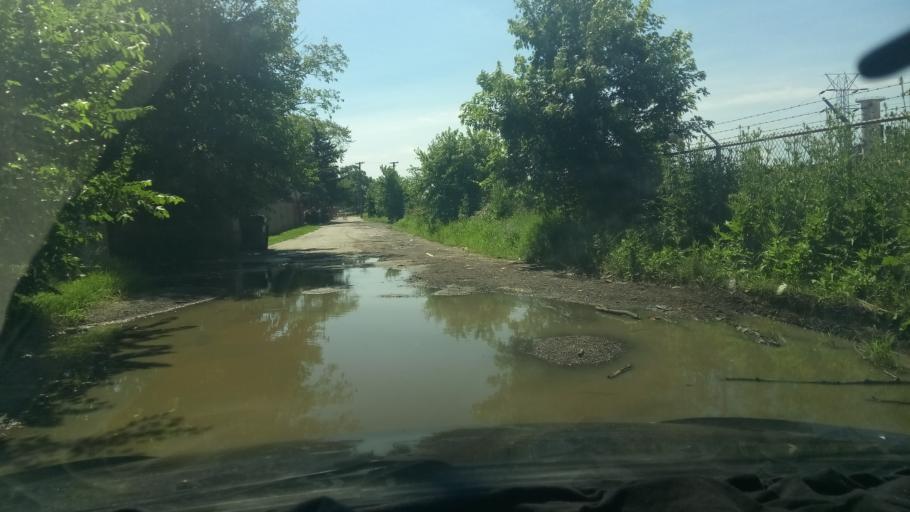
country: US
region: Illinois
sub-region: Cook County
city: Hometown
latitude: 41.7619
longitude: -87.7206
